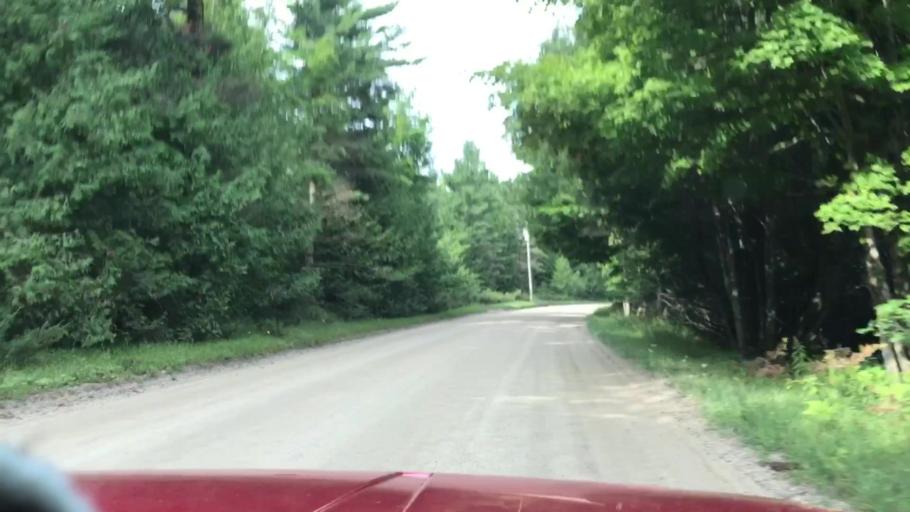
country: US
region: Michigan
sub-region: Charlevoix County
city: Charlevoix
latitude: 45.7280
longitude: -85.5328
